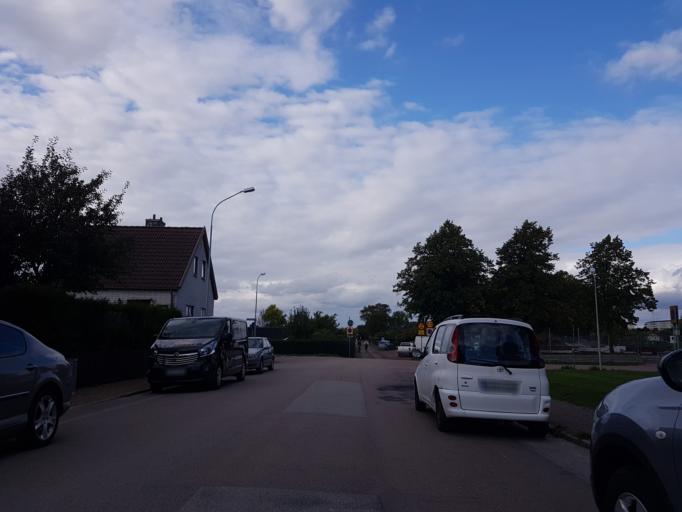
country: SE
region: Skane
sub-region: Landskrona
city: Landskrona
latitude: 55.8827
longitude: 12.8240
